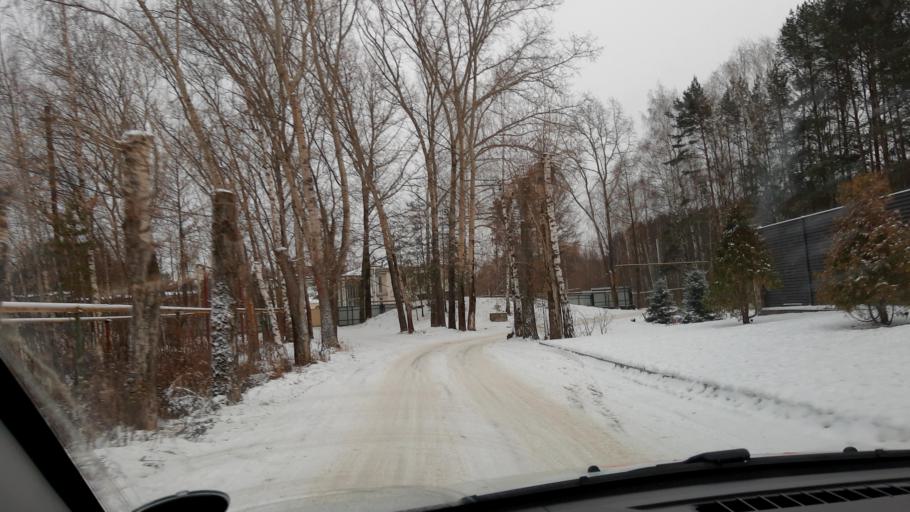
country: RU
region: Nizjnij Novgorod
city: Burevestnik
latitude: 56.1967
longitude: 43.7723
